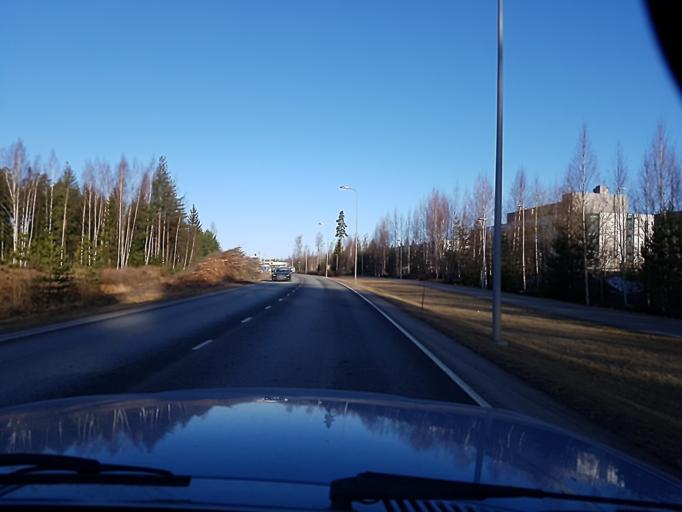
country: FI
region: Uusimaa
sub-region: Helsinki
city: Vantaa
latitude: 60.2931
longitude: 24.9292
